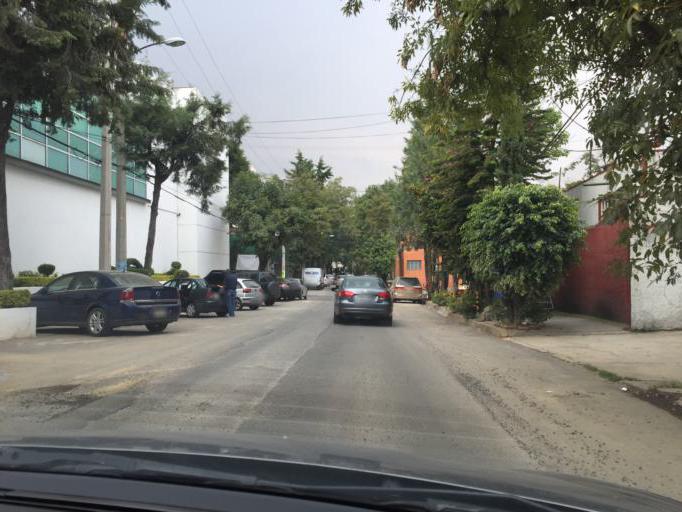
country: MX
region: Mexico City
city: Alvaro Obregon
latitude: 19.3760
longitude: -99.1931
